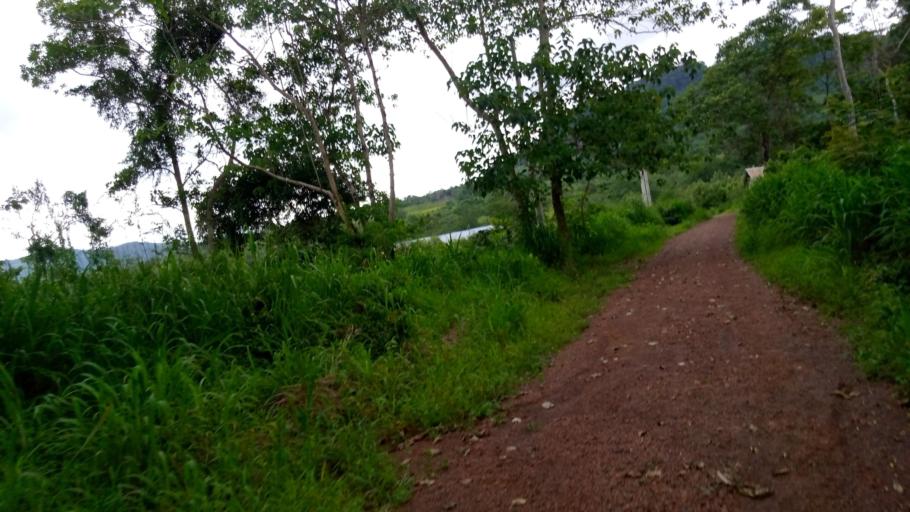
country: SL
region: Southern Province
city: Moyamba
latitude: 8.1586
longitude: -12.4459
